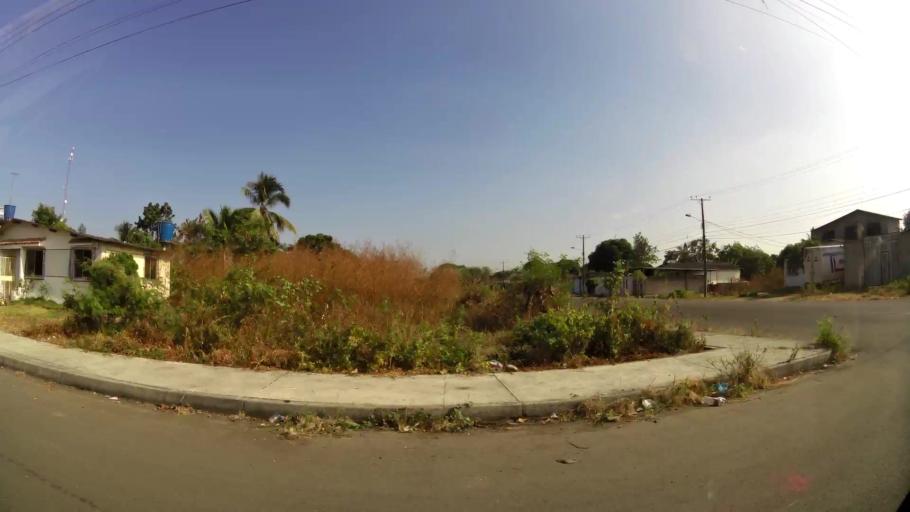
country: EC
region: Guayas
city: Eloy Alfaro
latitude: -2.2014
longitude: -79.8200
